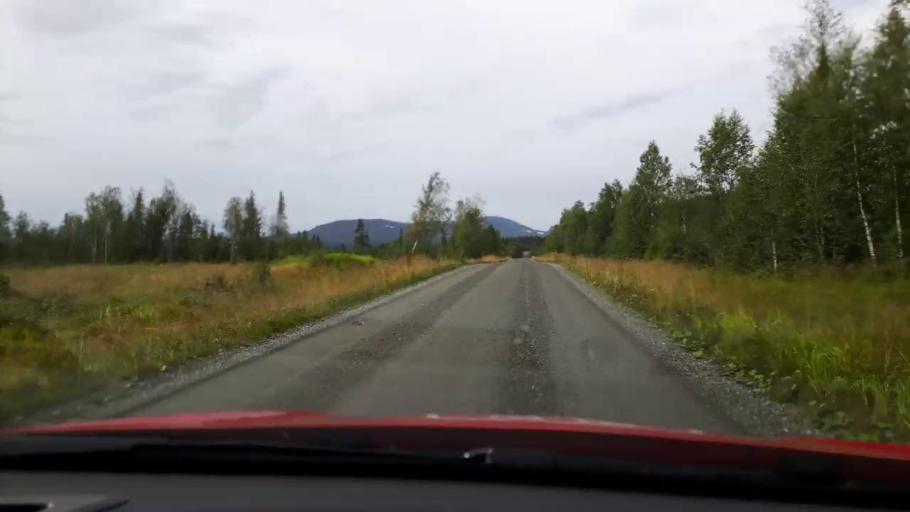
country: SE
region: Jaemtland
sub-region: Are Kommun
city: Are
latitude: 63.7419
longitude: 12.9994
